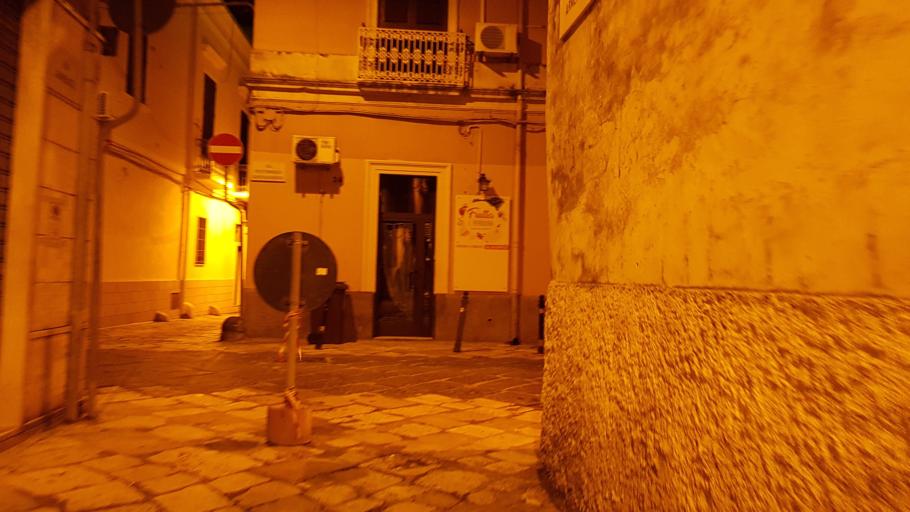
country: IT
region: Apulia
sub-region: Provincia di Brindisi
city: Brindisi
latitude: 40.6391
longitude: 17.9423
